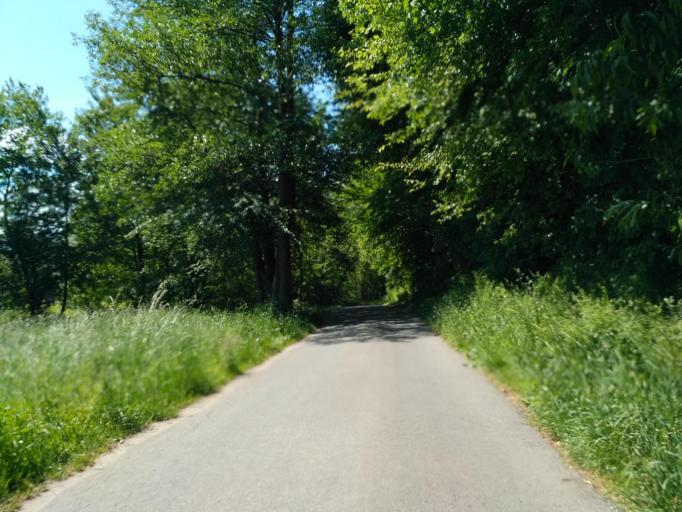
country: PL
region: Subcarpathian Voivodeship
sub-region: Powiat krosnienski
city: Miejsce Piastowe
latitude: 49.6516
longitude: 21.7596
